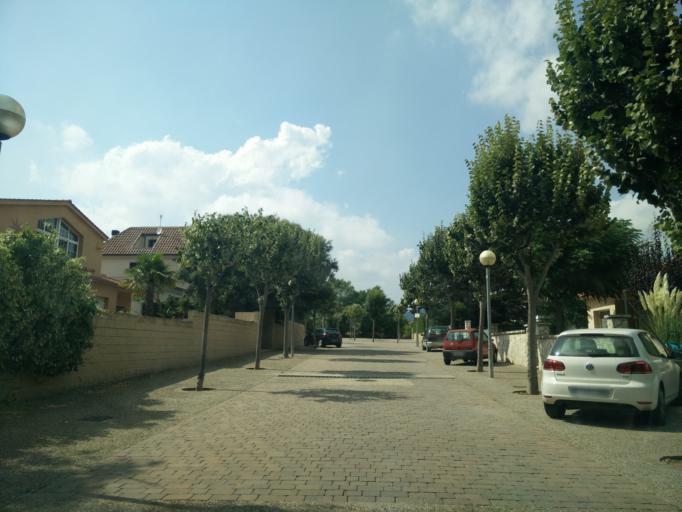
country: ES
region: Catalonia
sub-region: Provincia de Barcelona
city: Piera
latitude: 41.5397
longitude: 1.7643
